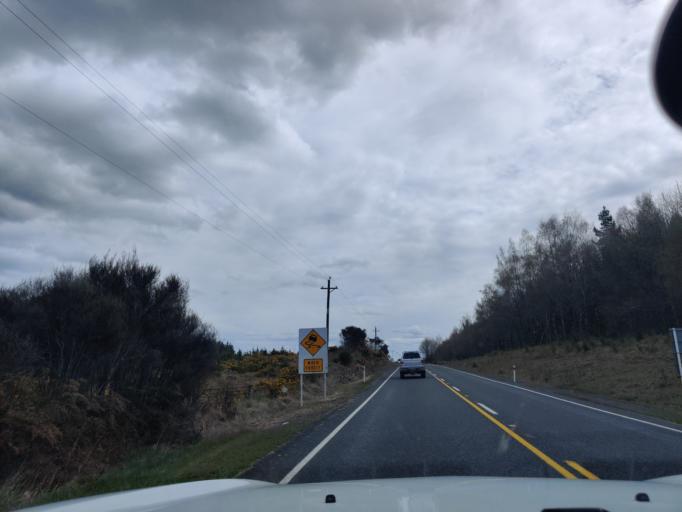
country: NZ
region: Manawatu-Wanganui
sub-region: Ruapehu District
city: Waiouru
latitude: -39.4711
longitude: 175.5547
